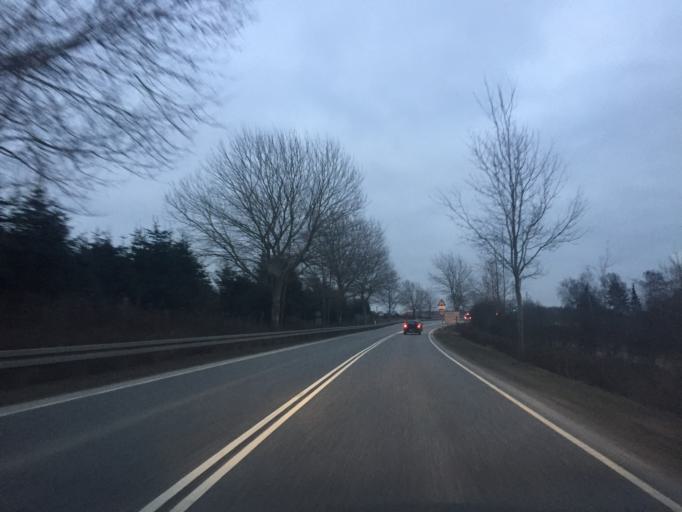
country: DK
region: Capital Region
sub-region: Frederikssund Kommune
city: Slangerup
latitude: 55.8489
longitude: 12.1445
